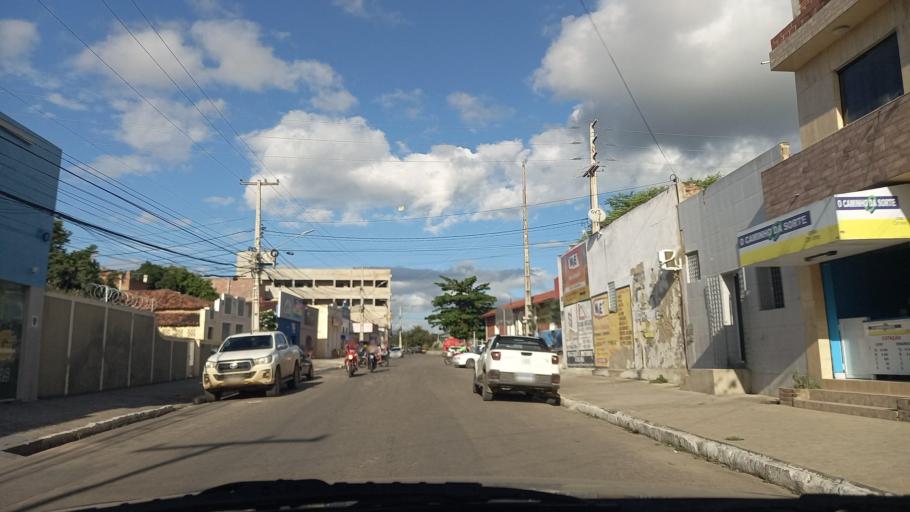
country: BR
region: Pernambuco
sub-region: Gravata
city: Gravata
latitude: -8.2043
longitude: -35.5734
